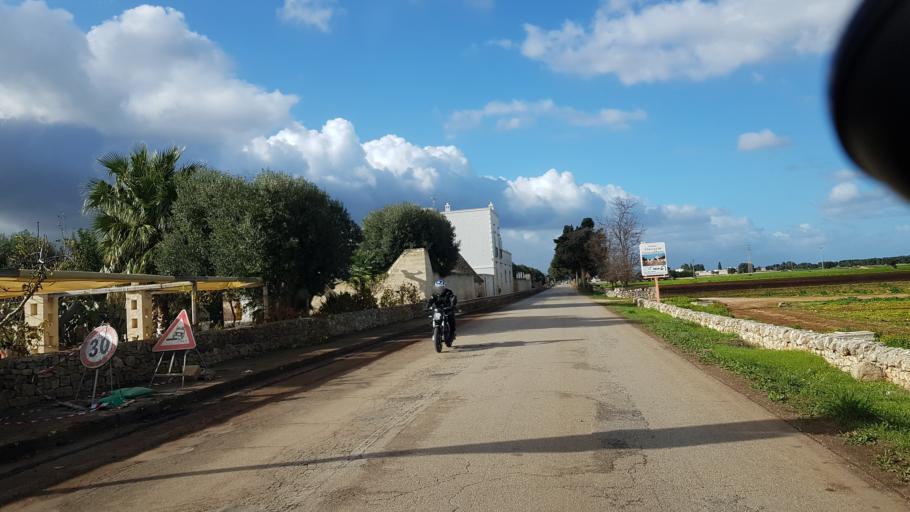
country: IT
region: Apulia
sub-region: Provincia di Brindisi
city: Montalbano
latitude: 40.7821
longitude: 17.4811
